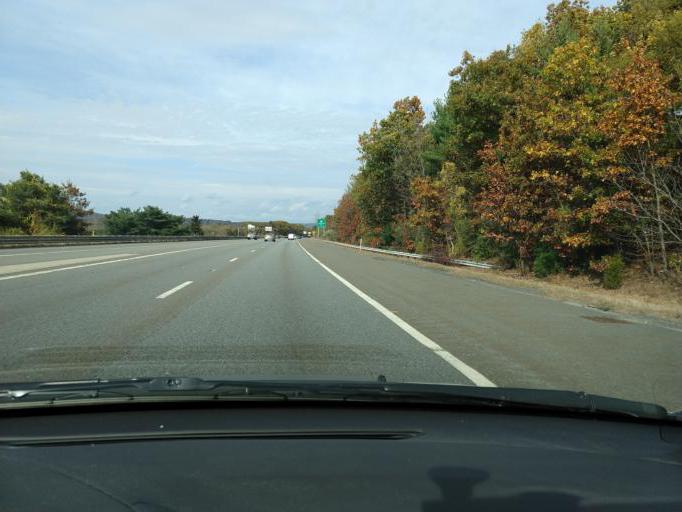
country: US
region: Massachusetts
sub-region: Worcester County
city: Leominster
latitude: 42.5269
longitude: -71.7309
